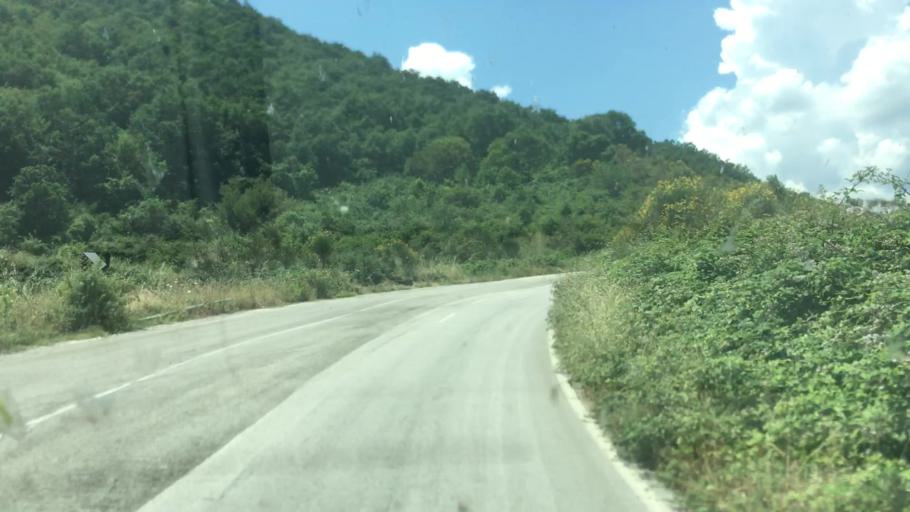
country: IT
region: Basilicate
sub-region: Provincia di Potenza
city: Tolve
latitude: 40.6863
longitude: 15.9830
